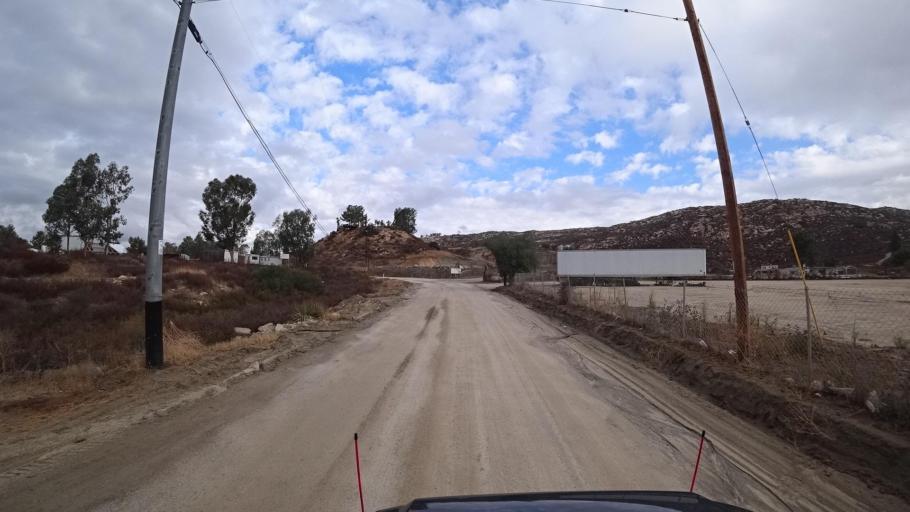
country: MX
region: Baja California
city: Tecate
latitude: 32.5873
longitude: -116.6208
